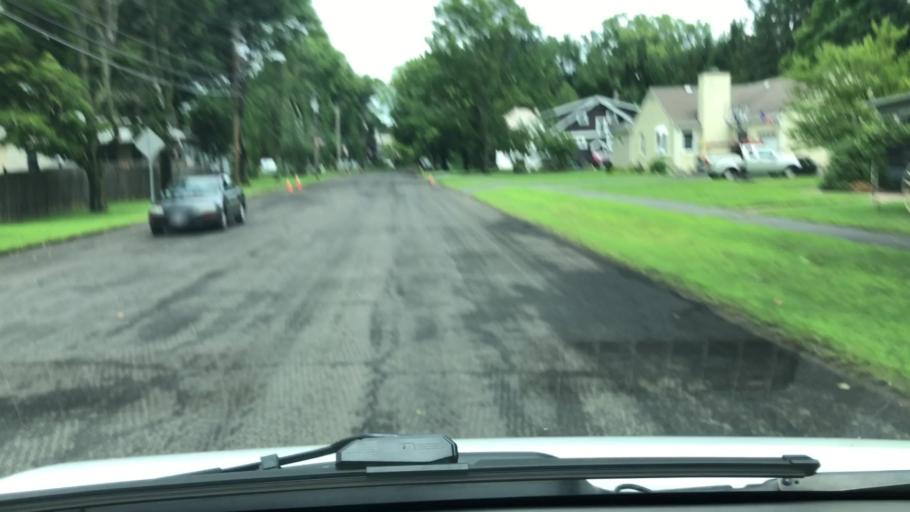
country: US
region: Massachusetts
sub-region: Franklin County
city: South Deerfield
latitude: 42.4731
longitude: -72.6108
